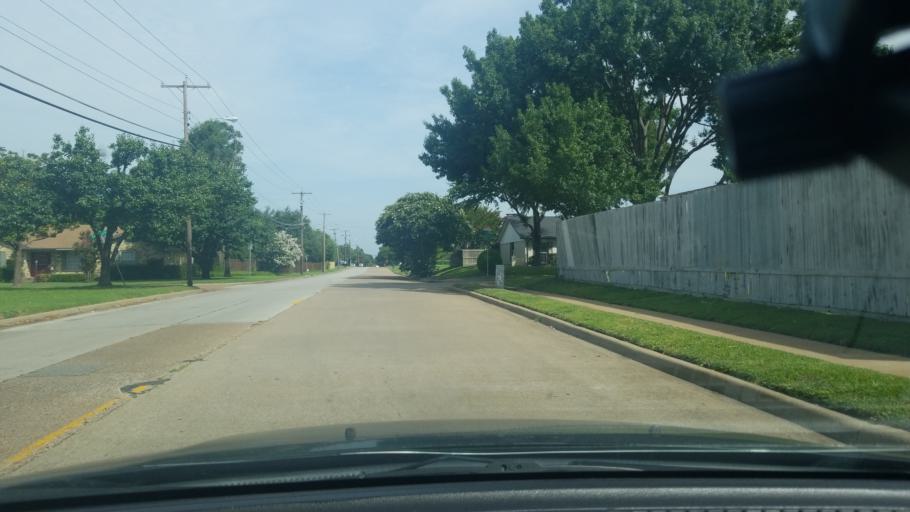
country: US
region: Texas
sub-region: Dallas County
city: Highland Park
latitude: 32.8020
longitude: -96.6957
